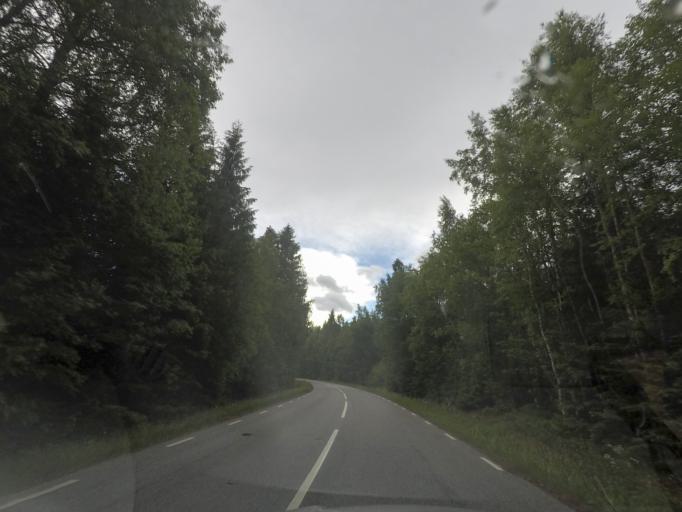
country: SE
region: Dalarna
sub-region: Ludvika Kommun
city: Grangesberg
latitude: 60.0607
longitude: 14.8815
